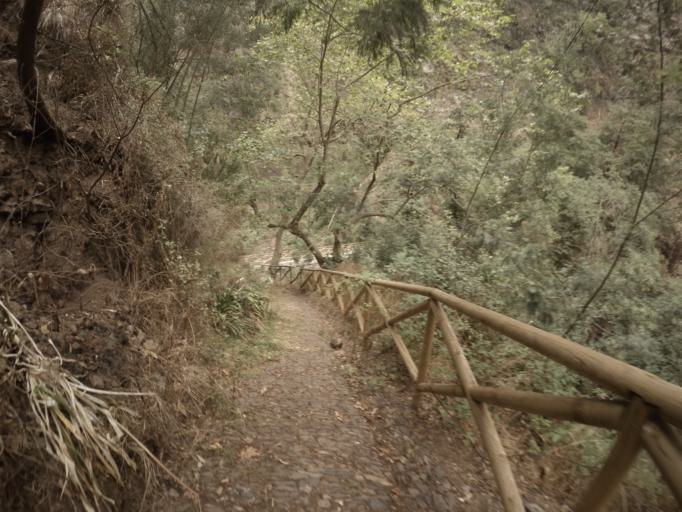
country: PT
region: Madeira
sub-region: Funchal
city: Nossa Senhora do Monte
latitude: 32.6888
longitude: -16.9110
